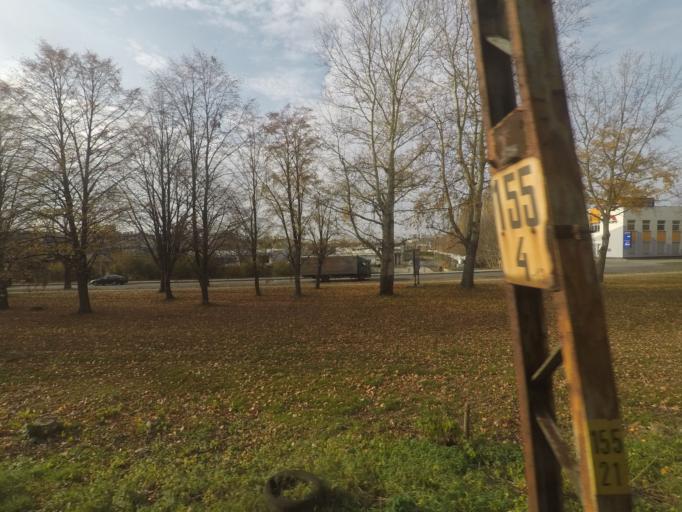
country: PL
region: Subcarpathian Voivodeship
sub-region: Rzeszow
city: Rzeszow
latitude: 50.0566
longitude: 21.9932
